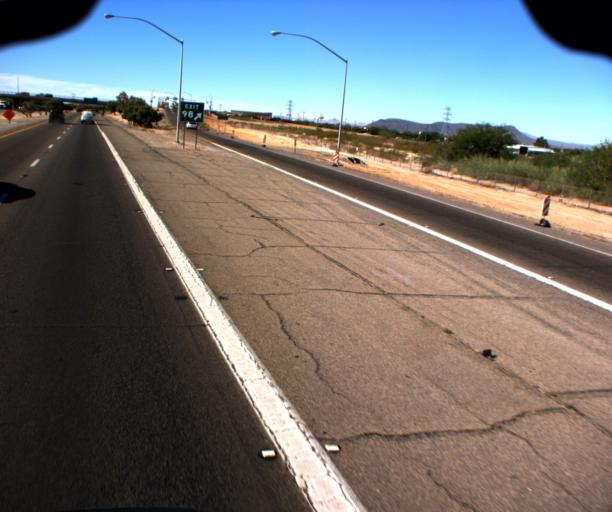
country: US
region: Arizona
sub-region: Pima County
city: South Tucson
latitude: 32.1667
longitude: -110.9858
